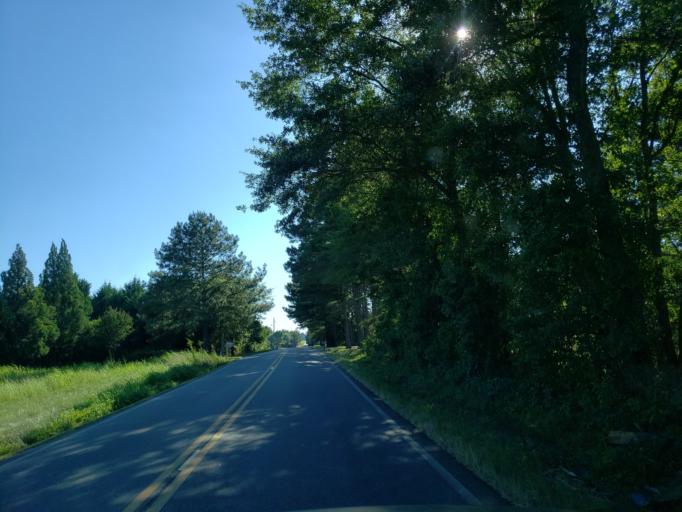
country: US
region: Georgia
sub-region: Bartow County
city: Euharlee
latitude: 34.1058
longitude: -84.9634
